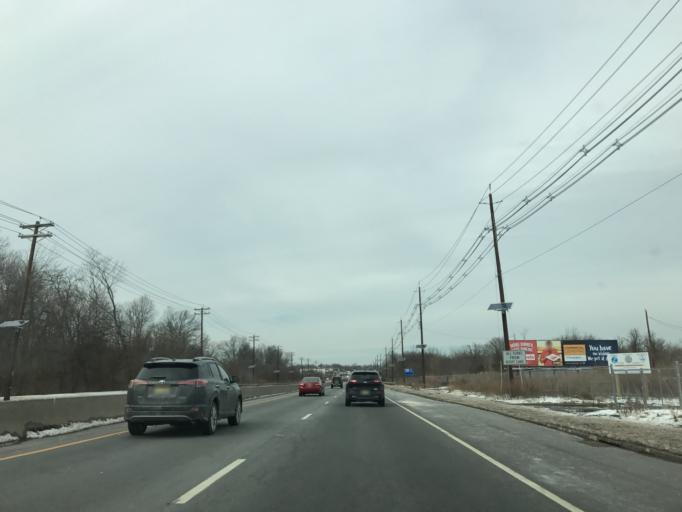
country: US
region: New Jersey
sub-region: Somerset County
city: Raritan
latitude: 40.5623
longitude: -74.6204
